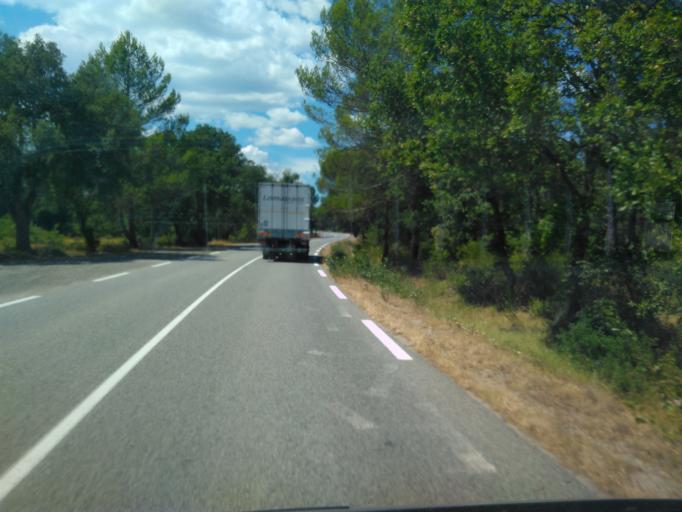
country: FR
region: Provence-Alpes-Cote d'Azur
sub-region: Departement du Var
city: Le Cannet-des-Maures
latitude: 43.3634
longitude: 6.3792
